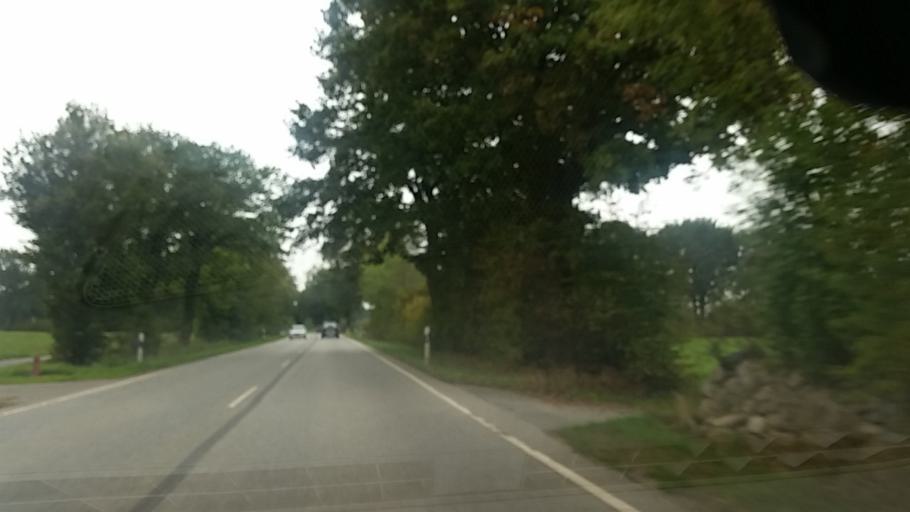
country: DE
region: Schleswig-Holstein
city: Kayhude
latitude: 53.7797
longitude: 10.1273
